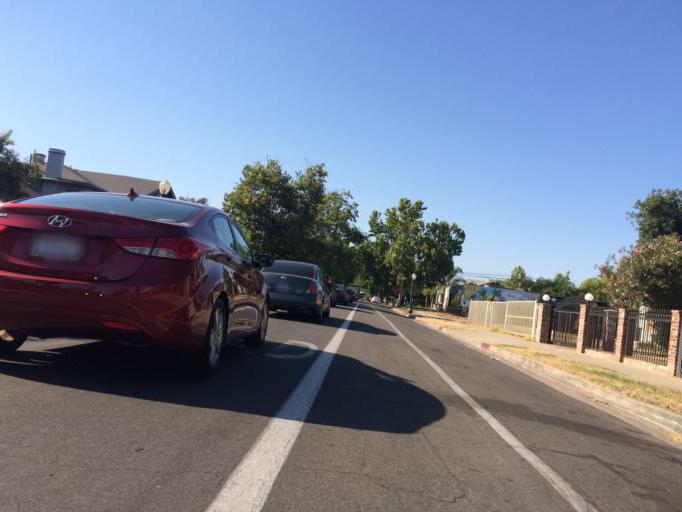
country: US
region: California
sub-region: Fresno County
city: Fresno
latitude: 36.7521
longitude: -119.7989
